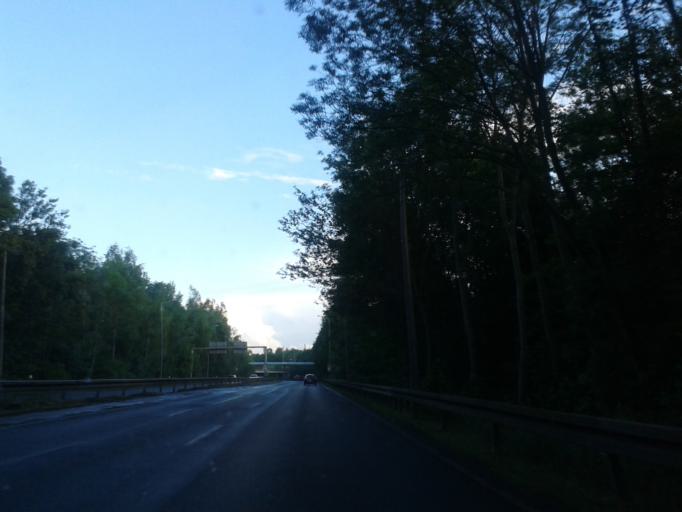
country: DE
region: Saxony
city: Markkleeberg
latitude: 51.2979
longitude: 12.3768
